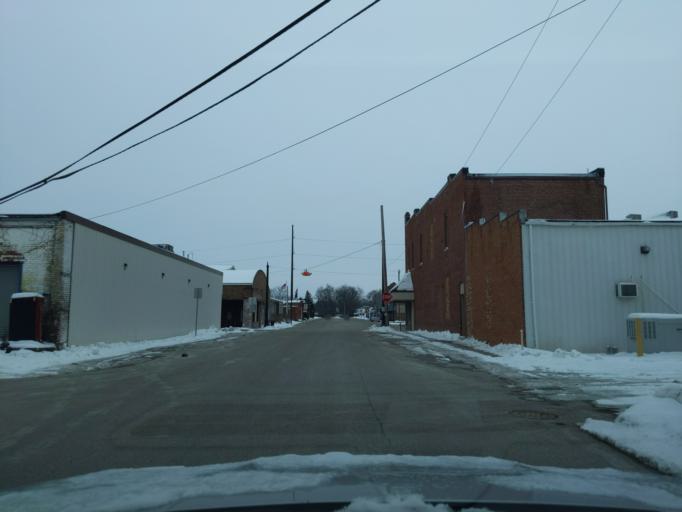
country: US
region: Indiana
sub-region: Benton County
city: Otterbein
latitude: 40.4909
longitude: -87.0962
